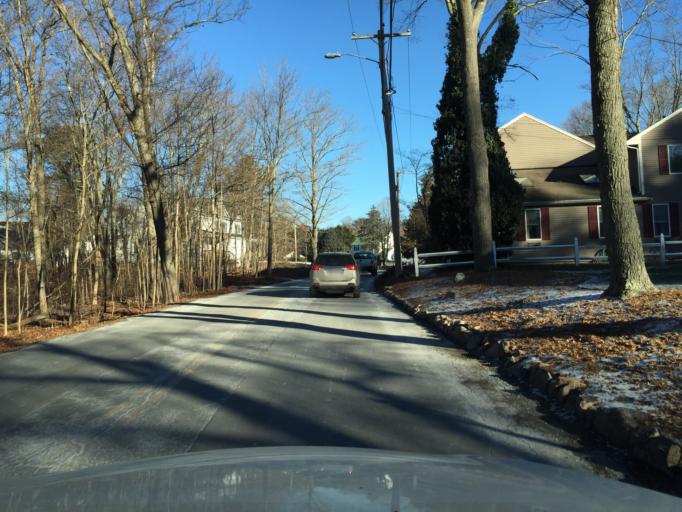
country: US
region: Massachusetts
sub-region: Norfolk County
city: Foxborough
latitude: 42.0617
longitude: -71.2356
